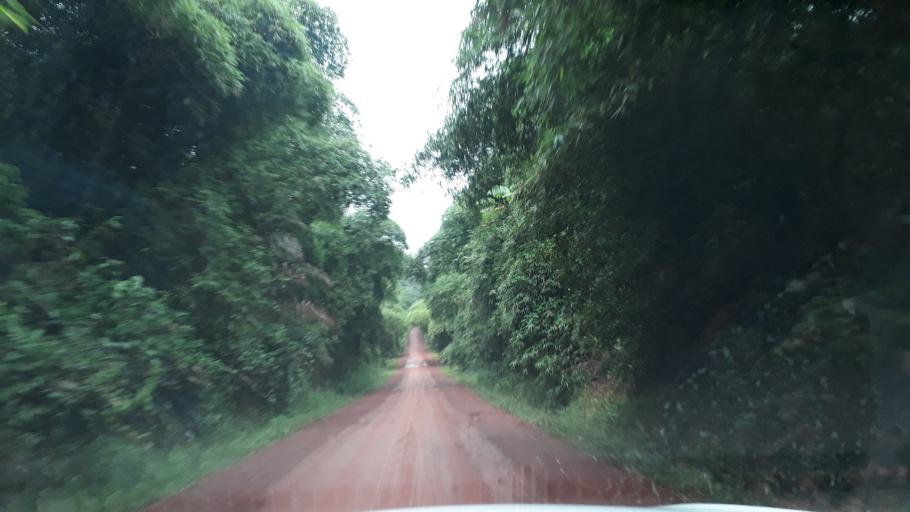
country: CD
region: Eastern Province
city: Wamba
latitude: 1.3493
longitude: 27.5885
